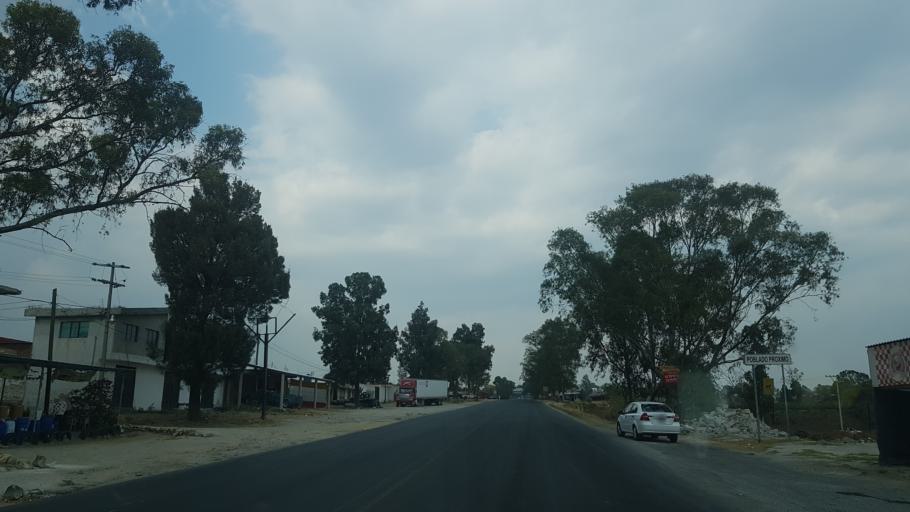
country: MX
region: Puebla
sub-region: Santa Isabel Cholula
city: San Pablo Ahuatempa
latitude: 18.9792
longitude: -98.3701
